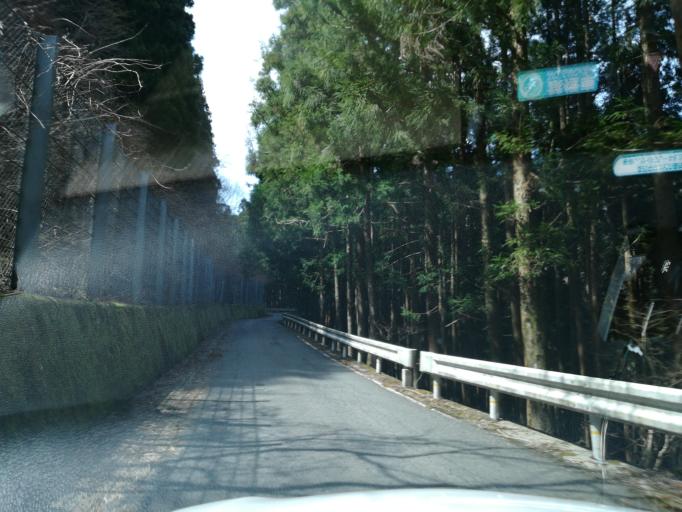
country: JP
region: Tokushima
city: Wakimachi
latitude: 33.8888
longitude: 134.0622
